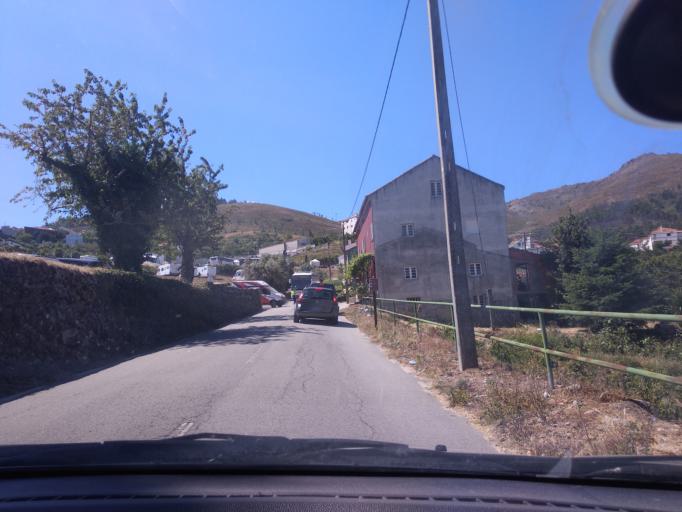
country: PT
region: Castelo Branco
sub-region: Concelho do Fundao
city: Fundao
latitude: 40.1195
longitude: -7.4843
